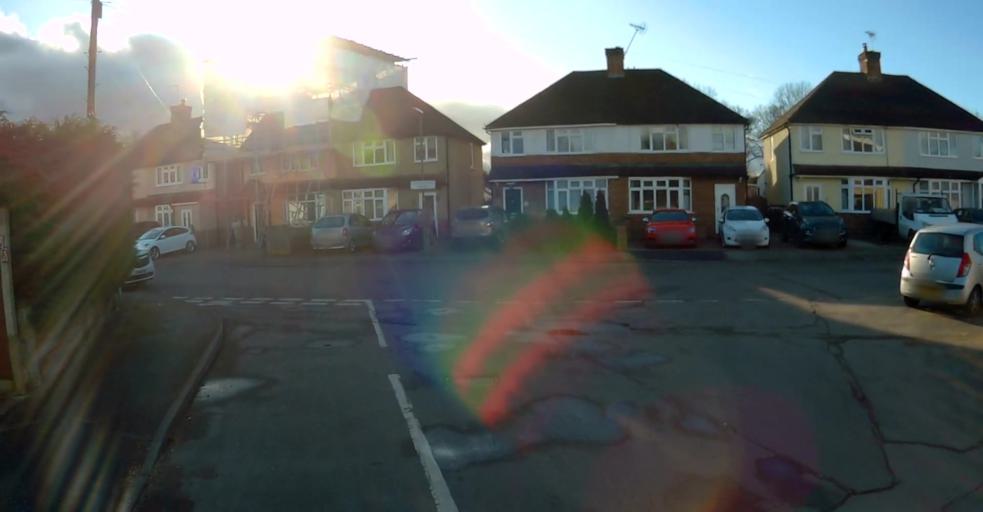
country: GB
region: England
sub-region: Surrey
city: Addlestone
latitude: 51.3710
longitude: -0.4783
